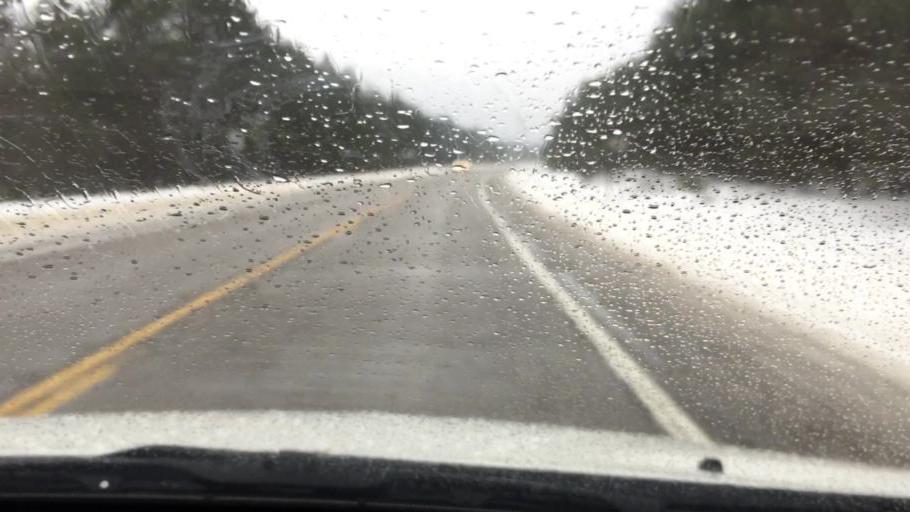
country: US
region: Michigan
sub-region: Charlevoix County
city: East Jordan
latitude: 45.0923
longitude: -85.0966
